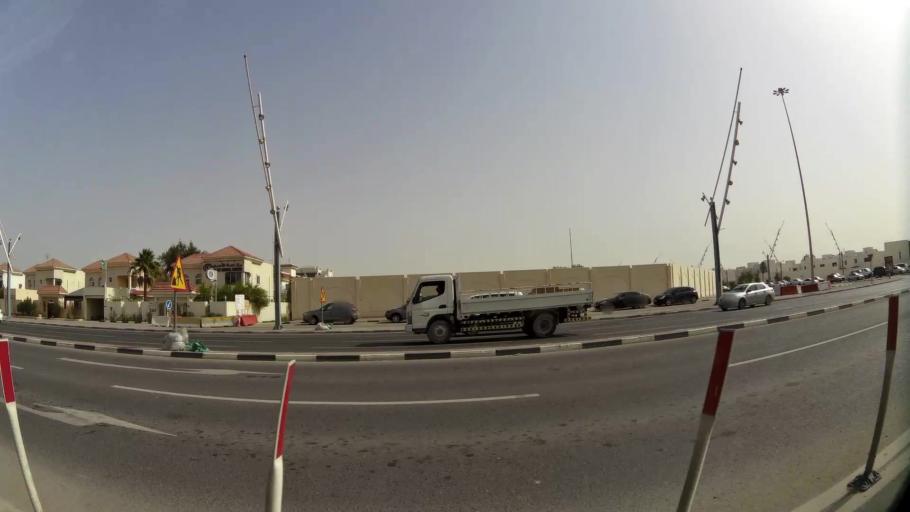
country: QA
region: Baladiyat ar Rayyan
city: Ar Rayyan
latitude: 25.2655
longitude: 51.4645
